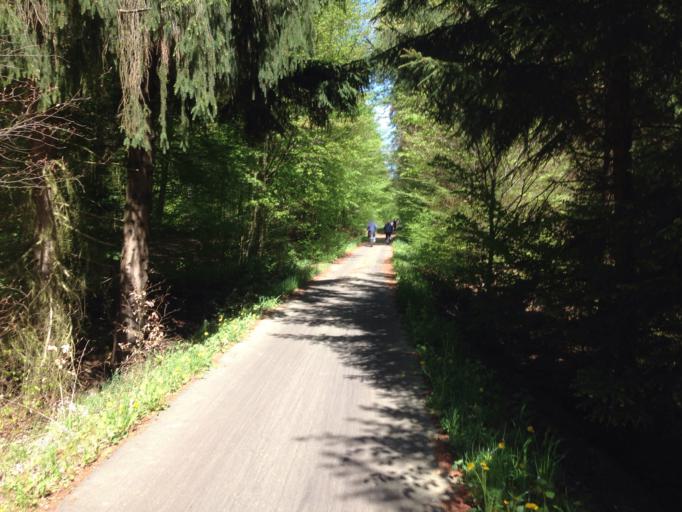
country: DE
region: Hesse
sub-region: Regierungsbezirk Giessen
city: Hungen
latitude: 50.5005
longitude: 8.9096
